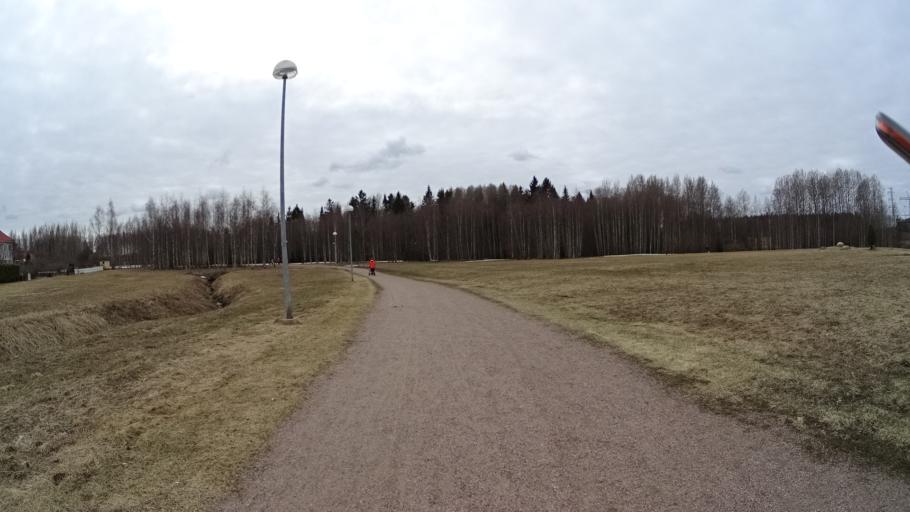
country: FI
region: Uusimaa
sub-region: Helsinki
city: Vantaa
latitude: 60.2888
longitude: 24.9399
